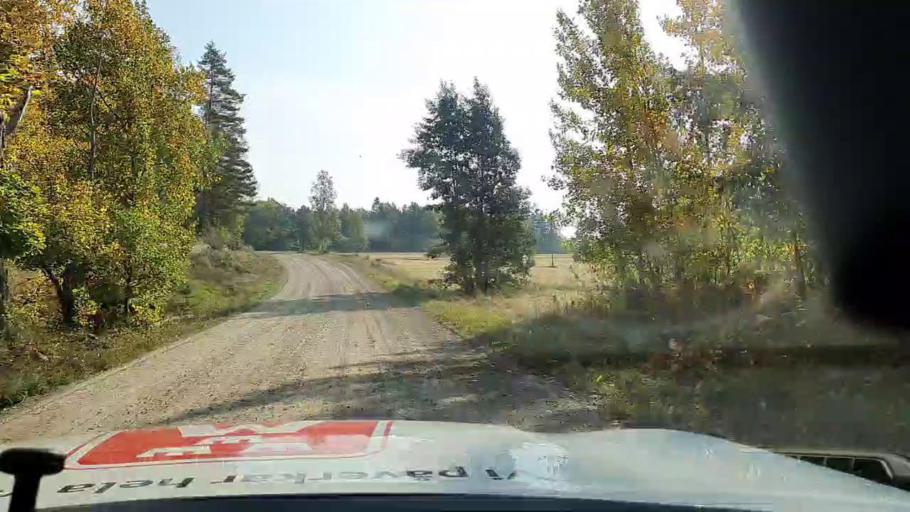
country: SE
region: Soedermanland
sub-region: Eskilstuna Kommun
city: Kvicksund
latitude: 59.3242
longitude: 16.2383
